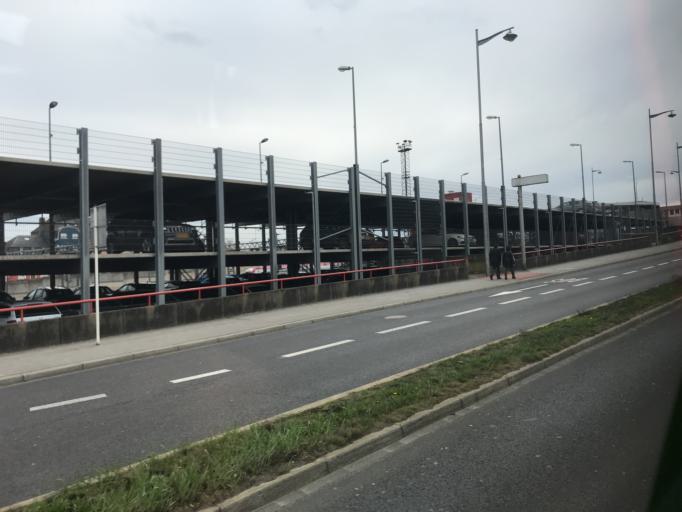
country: LU
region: Luxembourg
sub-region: Canton de Luxembourg
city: Luxembourg
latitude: 49.5973
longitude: 6.1319
